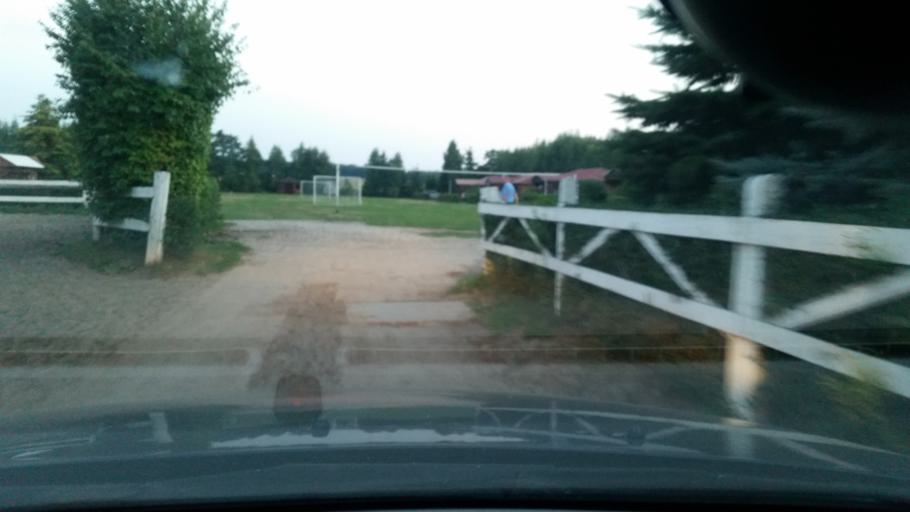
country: PL
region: Pomeranian Voivodeship
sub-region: Powiat wejherowski
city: Choczewo
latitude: 54.7691
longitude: 17.7973
